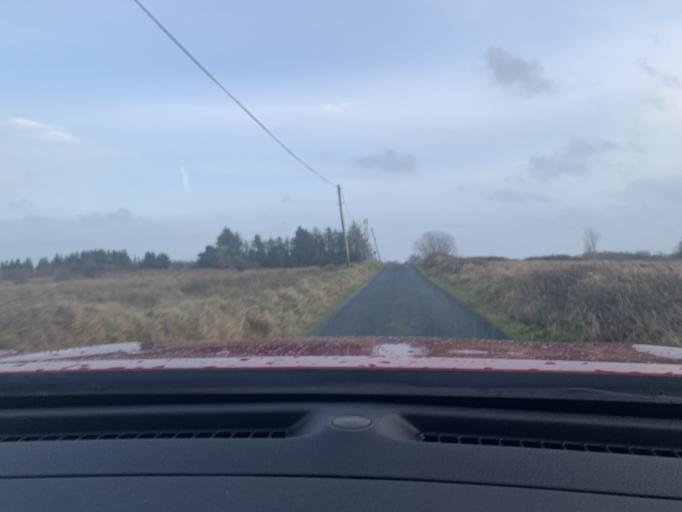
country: IE
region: Connaught
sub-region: Roscommon
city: Ballaghaderreen
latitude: 53.9579
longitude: -8.5363
